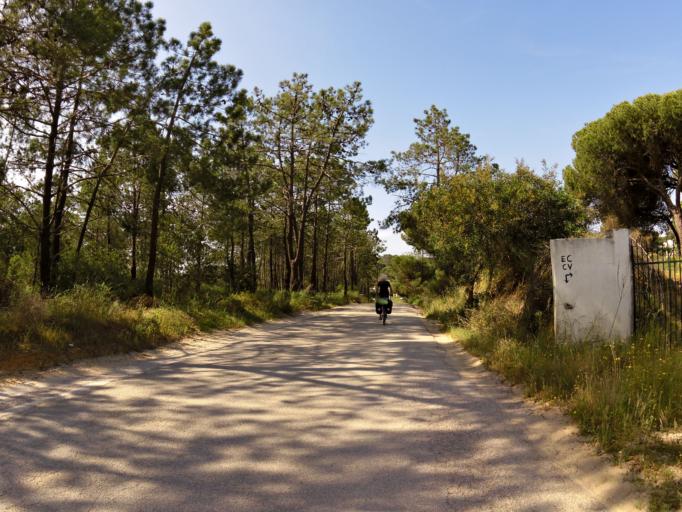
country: PT
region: Faro
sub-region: Loule
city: Almancil
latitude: 37.0603
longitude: -8.0161
